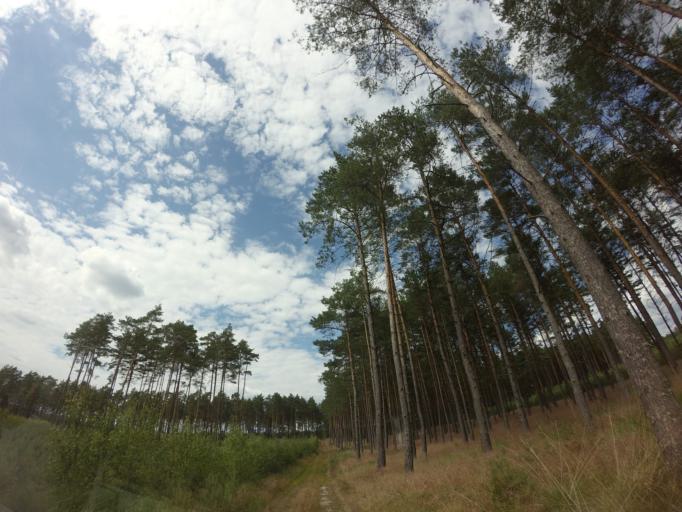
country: PL
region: West Pomeranian Voivodeship
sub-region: Powiat choszczenski
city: Drawno
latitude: 53.1576
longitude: 15.7373
